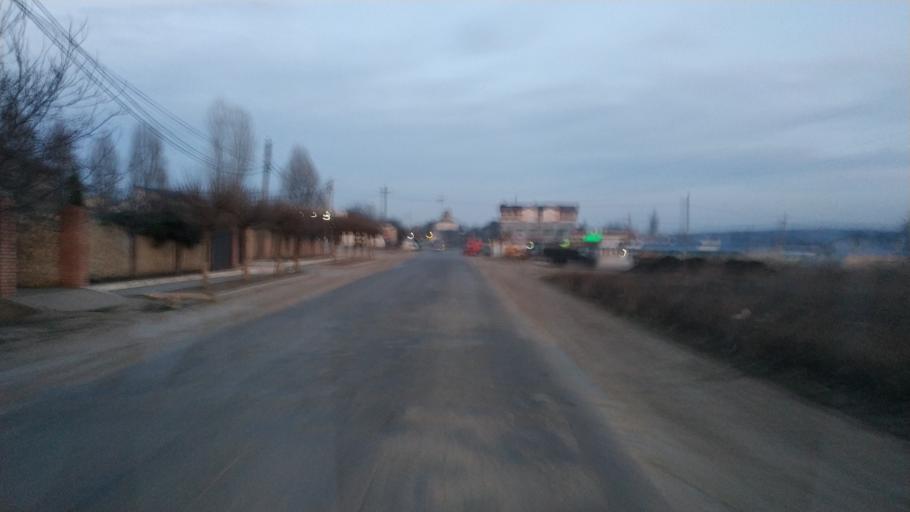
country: MD
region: Laloveni
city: Ialoveni
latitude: 46.9448
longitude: 28.7742
